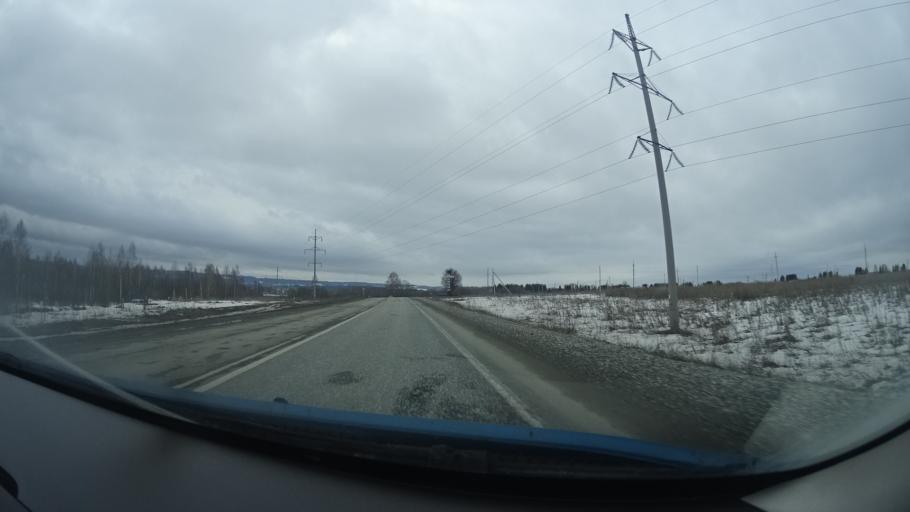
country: RU
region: Perm
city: Barda
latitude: 56.9489
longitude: 55.5853
